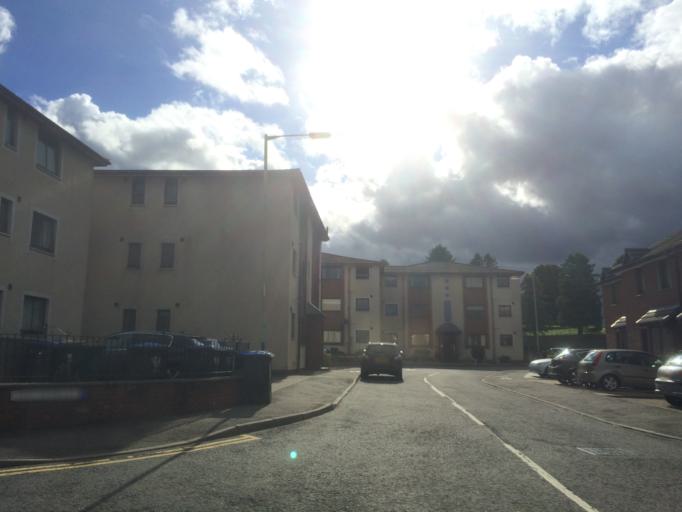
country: GB
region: Scotland
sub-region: Perth and Kinross
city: Perth
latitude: 56.4011
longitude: -3.4468
